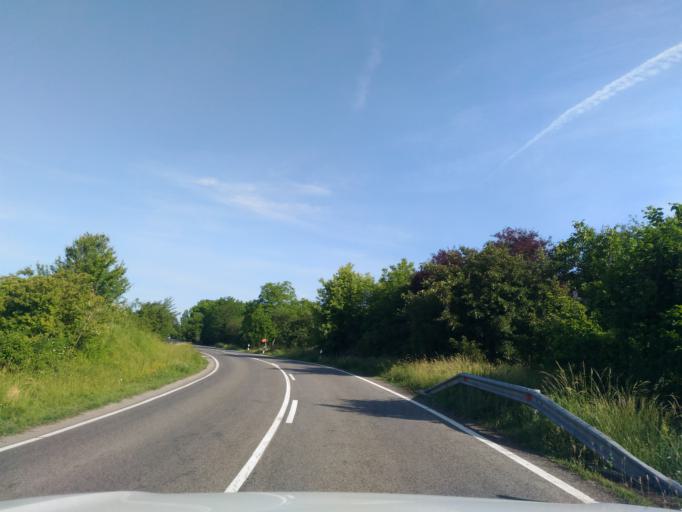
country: HU
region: Baranya
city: Komlo
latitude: 46.1732
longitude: 18.2628
